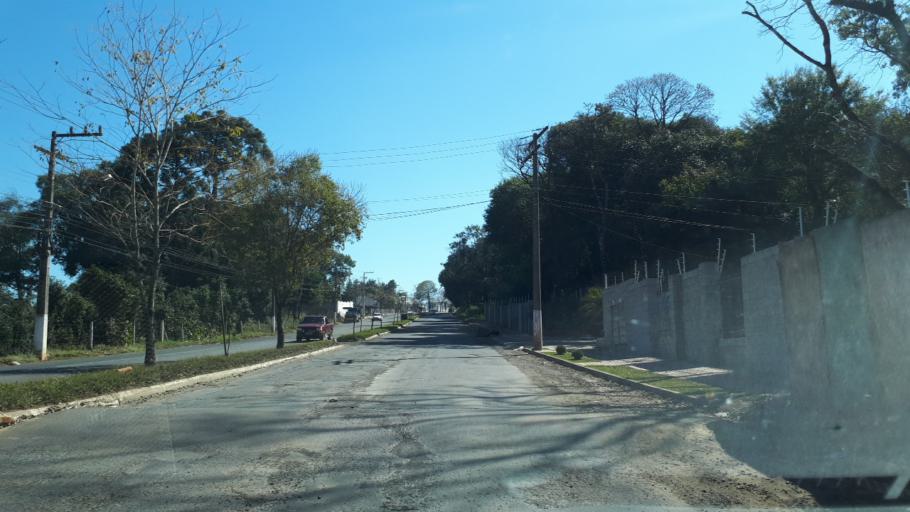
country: BR
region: Santa Catarina
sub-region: Chapeco
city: Chapeco
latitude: -27.1290
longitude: -52.6042
